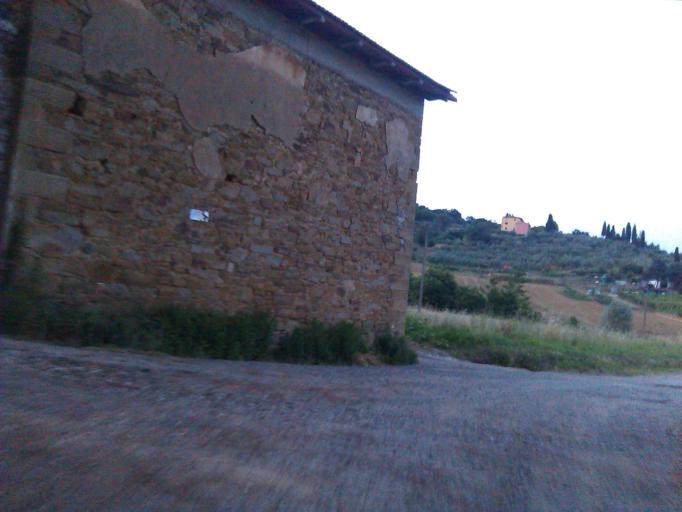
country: IT
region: Tuscany
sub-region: Province of Arezzo
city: Viciomaggio
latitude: 43.4440
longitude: 11.7749
